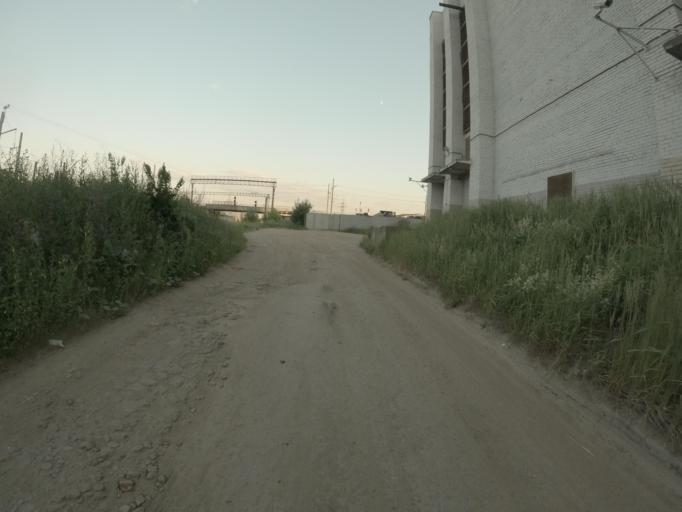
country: RU
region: St.-Petersburg
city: Admiralteisky
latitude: 59.8833
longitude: 30.2933
